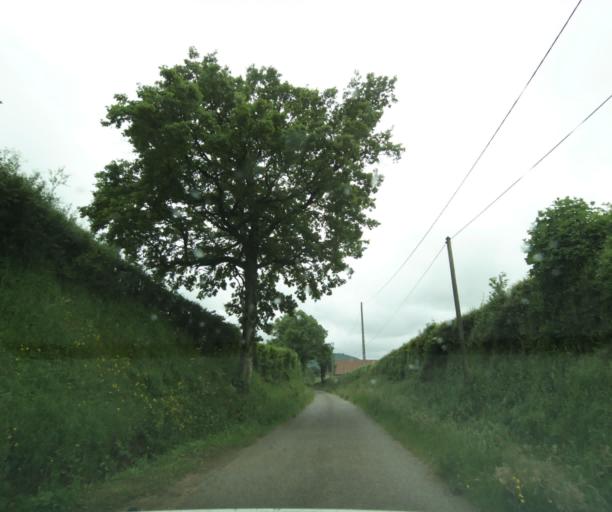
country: FR
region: Bourgogne
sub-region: Departement de Saone-et-Loire
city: Matour
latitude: 46.4374
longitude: 4.4450
